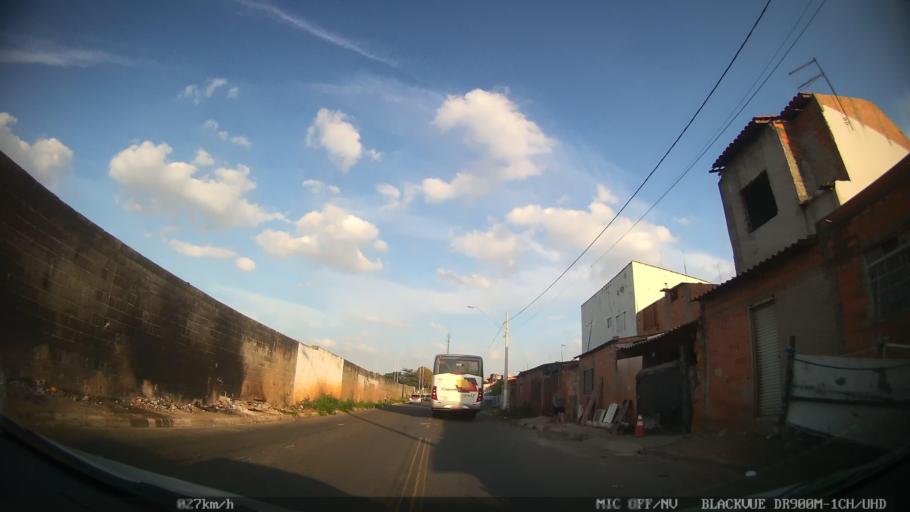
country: BR
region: Sao Paulo
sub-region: Hortolandia
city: Hortolandia
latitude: -22.8831
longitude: -47.1611
